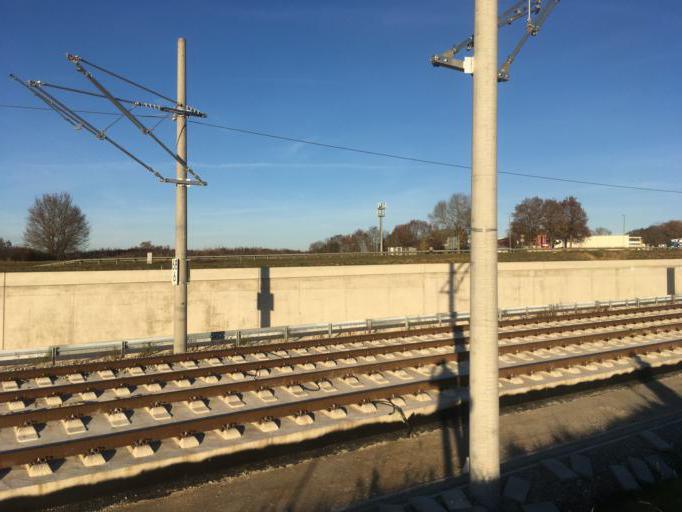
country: DE
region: Baden-Wuerttemberg
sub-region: Tuebingen Region
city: Nellingen
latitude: 48.5198
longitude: 9.8035
